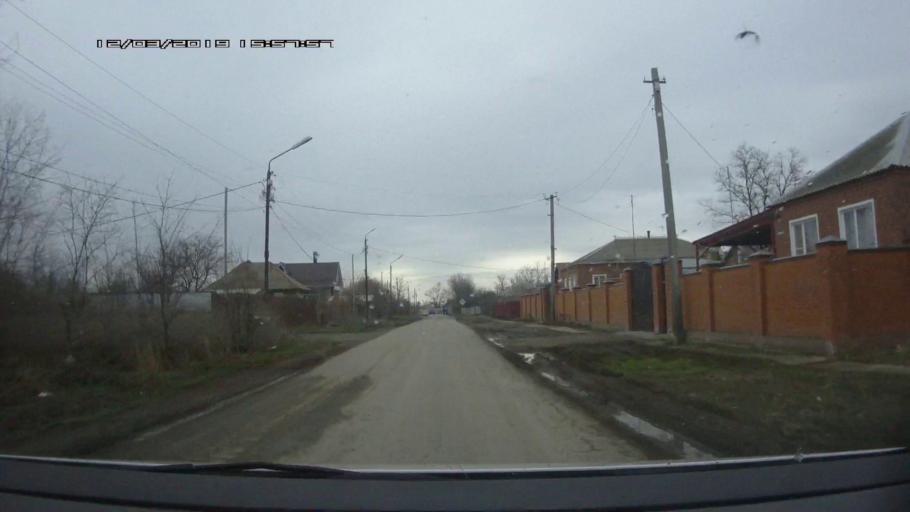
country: RU
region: Rostov
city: Novobataysk
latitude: 46.9027
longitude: 39.7878
